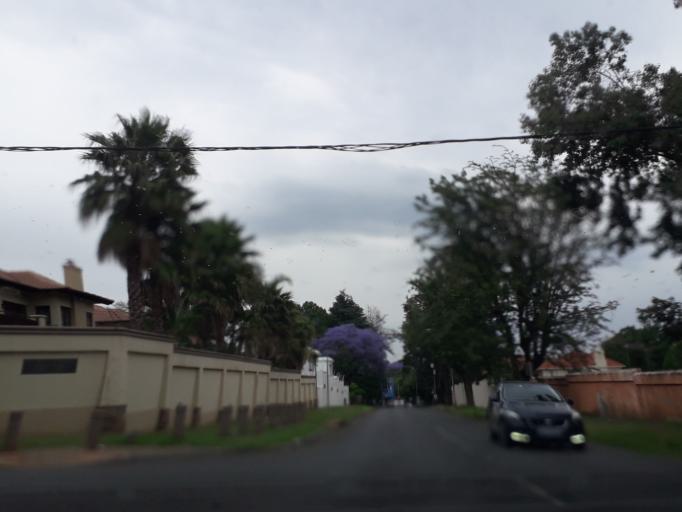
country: ZA
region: Gauteng
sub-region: City of Johannesburg Metropolitan Municipality
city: Johannesburg
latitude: -26.1688
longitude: 28.0585
